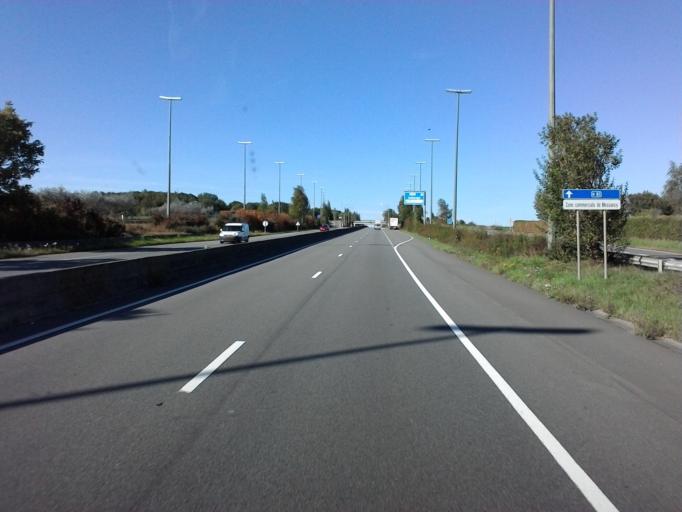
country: BE
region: Wallonia
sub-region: Province du Luxembourg
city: Messancy
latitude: 49.5830
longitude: 5.8091
